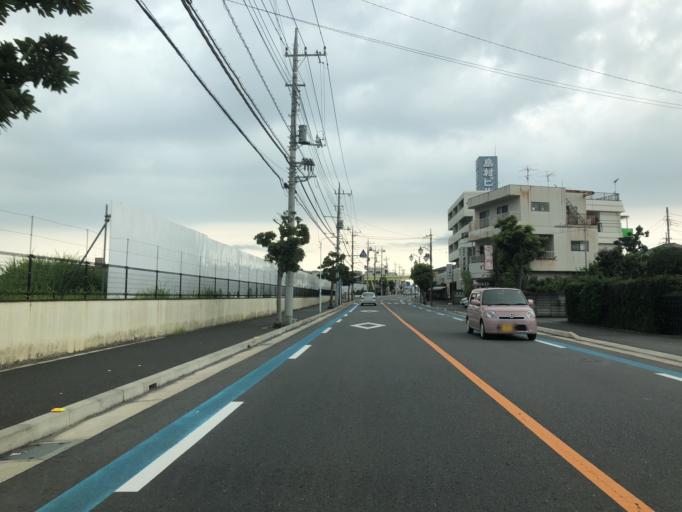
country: JP
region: Saitama
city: Sakado
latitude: 36.0304
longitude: 139.4055
